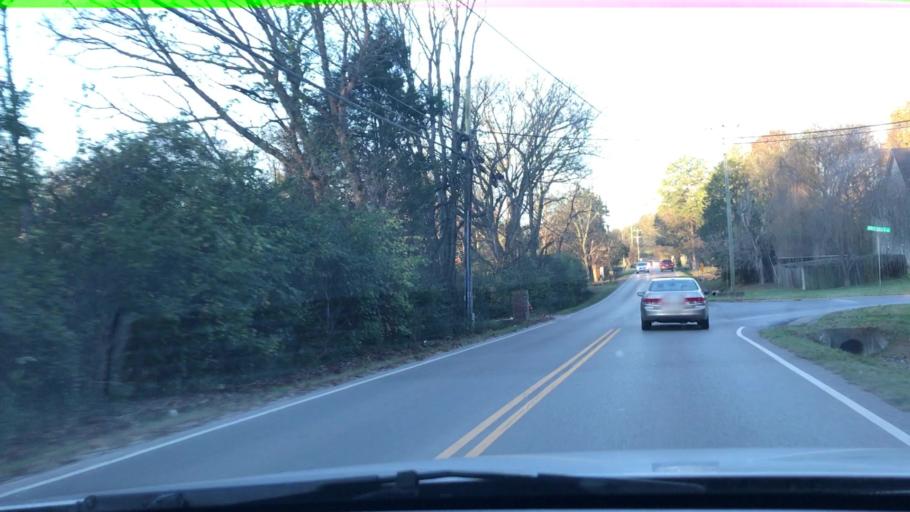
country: US
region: Tennessee
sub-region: Williamson County
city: Brentwood Estates
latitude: 36.0147
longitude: -86.7252
